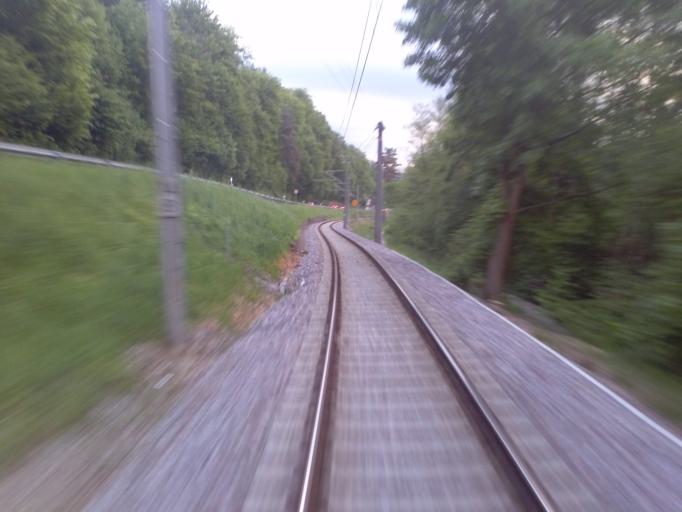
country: DE
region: Baden-Wuerttemberg
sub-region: Karlsruhe Region
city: Ettlingen
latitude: 48.8926
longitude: 8.4503
